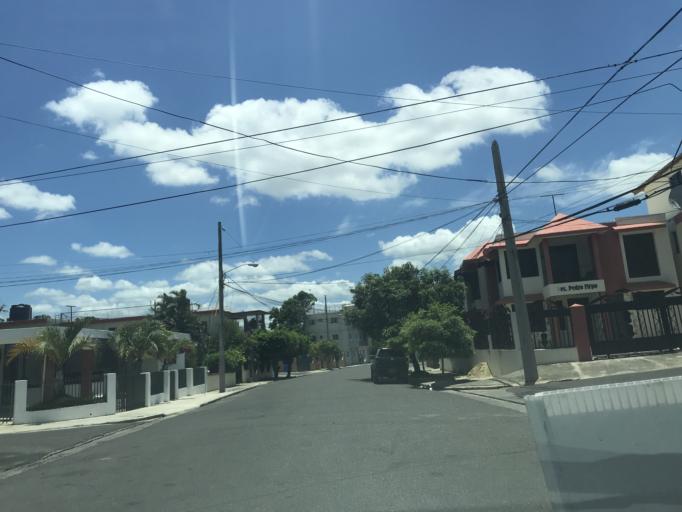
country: DO
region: Santiago
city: Santiago de los Caballeros
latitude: 19.4388
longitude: -70.6960
